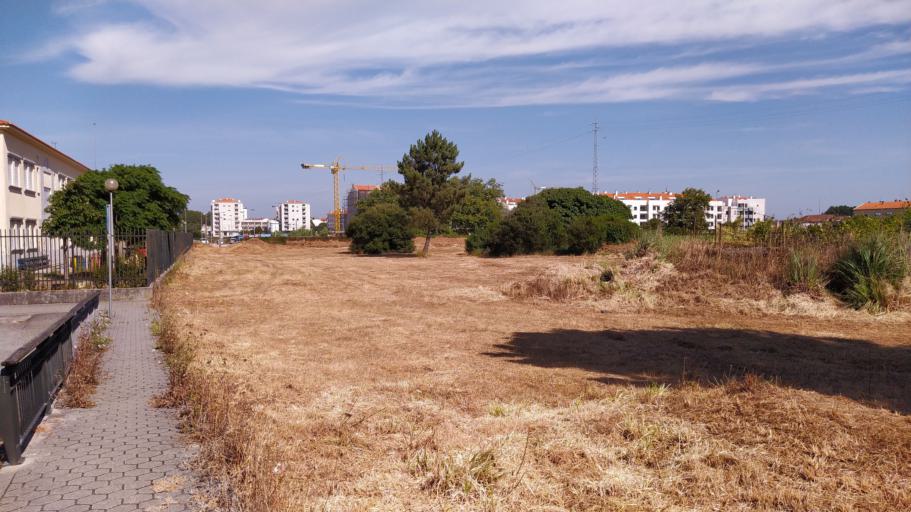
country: PT
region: Aveiro
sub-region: Aveiro
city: Aveiro
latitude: 40.6497
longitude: -8.6412
